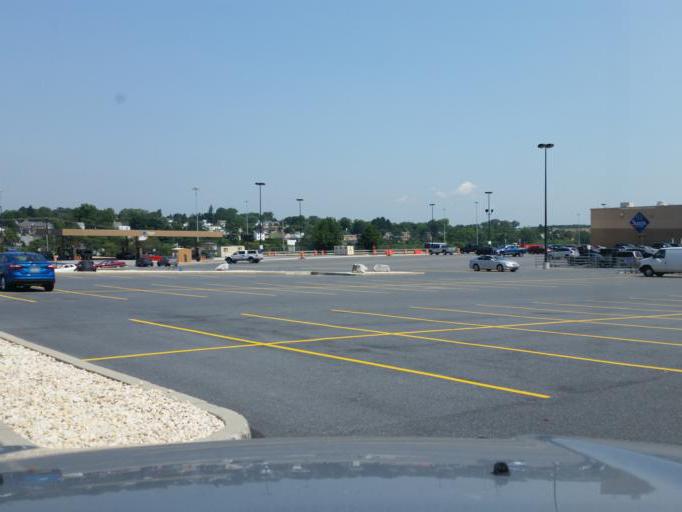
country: US
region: Pennsylvania
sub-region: Dauphin County
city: Rutherford
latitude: 40.2608
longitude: -76.7711
